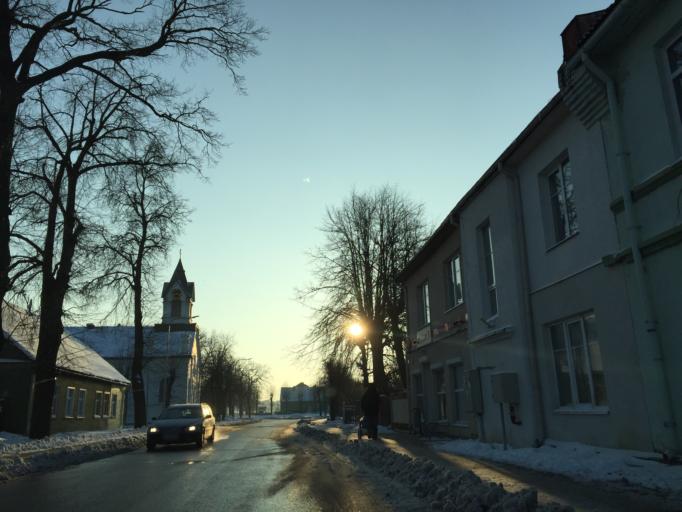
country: LV
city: Tireli
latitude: 56.9436
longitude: 23.6183
